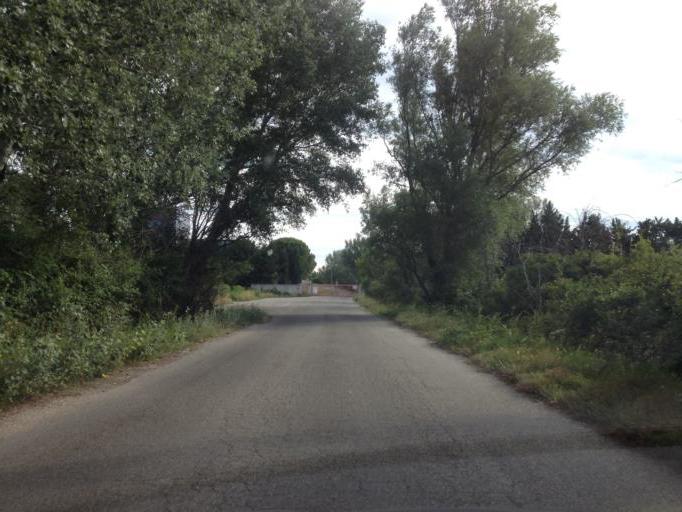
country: FR
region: Provence-Alpes-Cote d'Azur
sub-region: Departement du Vaucluse
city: Orange
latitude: 44.1229
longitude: 4.7953
